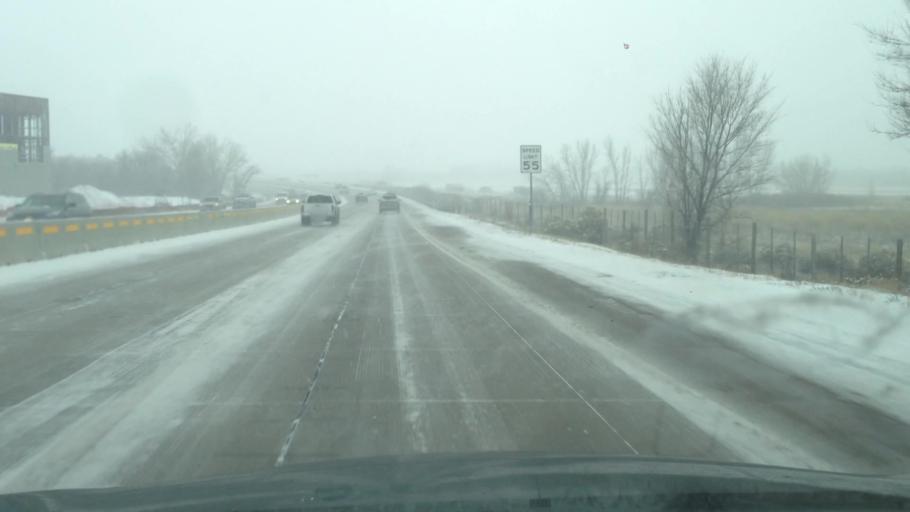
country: US
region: Colorado
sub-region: Arapahoe County
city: Dove Valley
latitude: 39.6205
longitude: -104.8205
